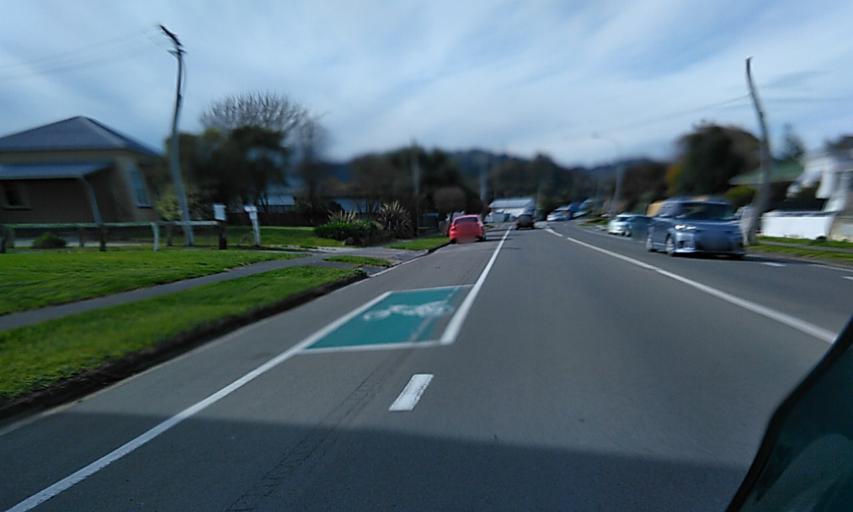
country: NZ
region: Gisborne
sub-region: Gisborne District
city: Gisborne
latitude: -38.6567
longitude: 178.0176
